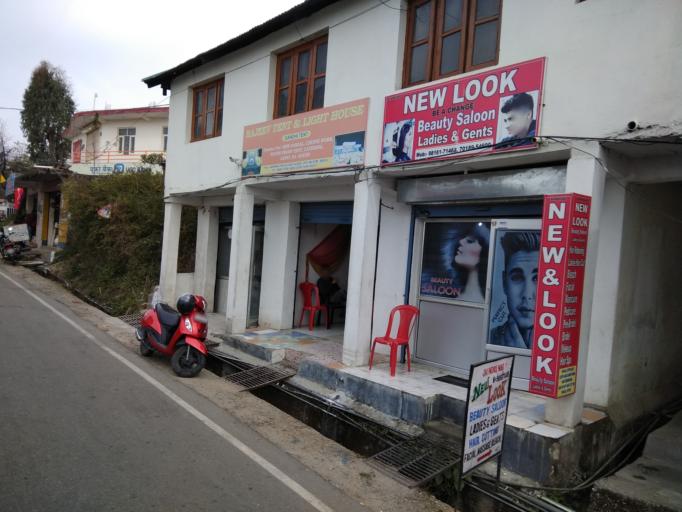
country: IN
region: Himachal Pradesh
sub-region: Kangra
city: Dharmsala
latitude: 32.2038
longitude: 76.3304
